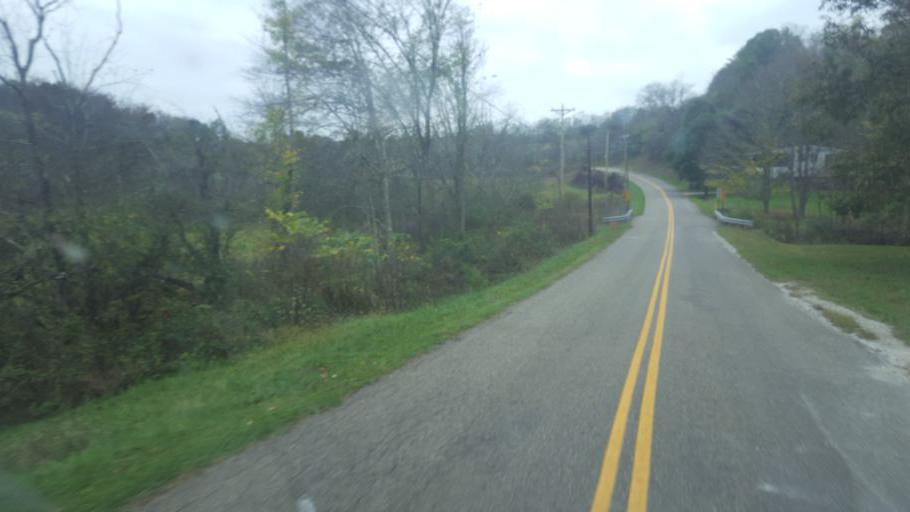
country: US
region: Ohio
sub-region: Carroll County
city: Carrollton
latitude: 40.4806
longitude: -81.0988
